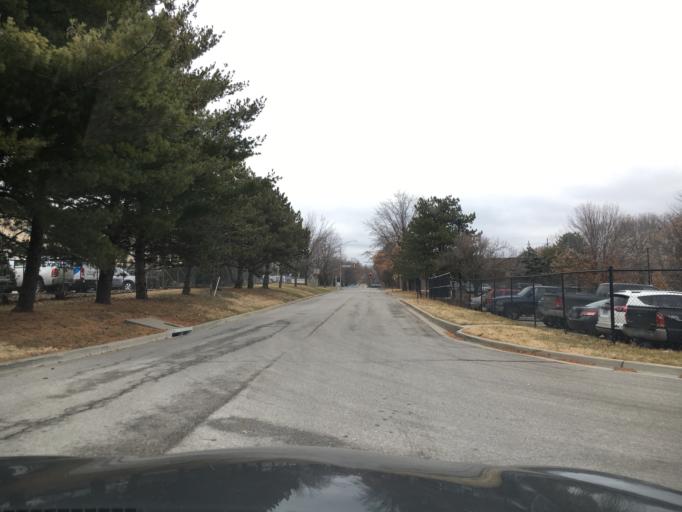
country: US
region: Kansas
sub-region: Johnson County
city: Lenexa
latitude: 38.9113
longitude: -94.6804
